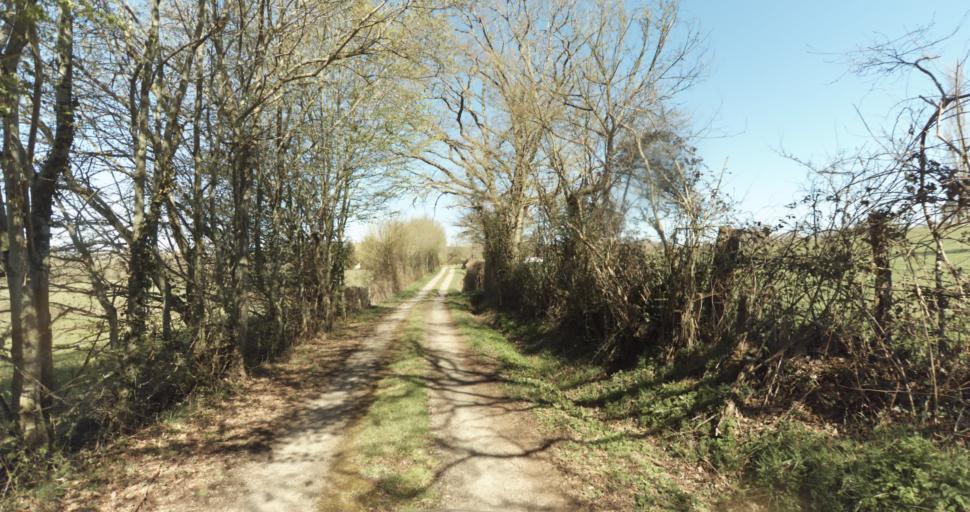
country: FR
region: Lower Normandy
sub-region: Departement du Calvados
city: Livarot
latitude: 49.0183
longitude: 0.0745
